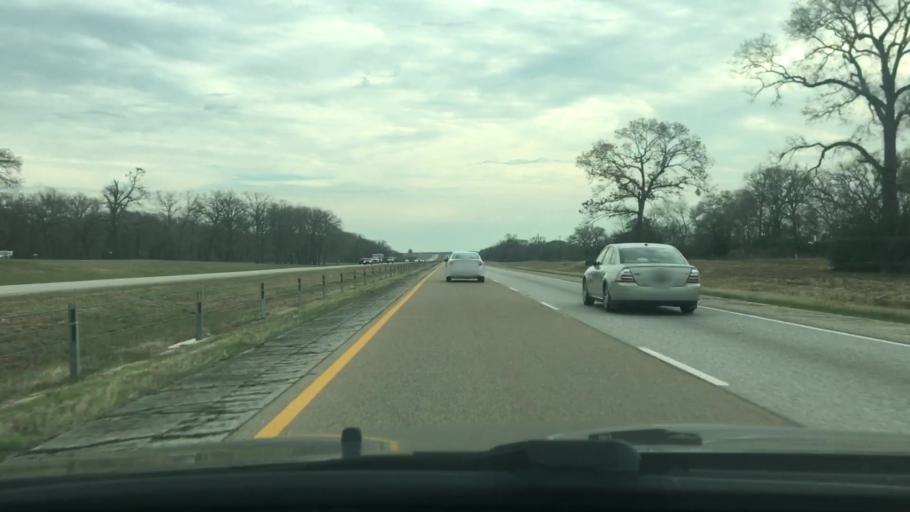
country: US
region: Texas
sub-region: Leon County
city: Centerville
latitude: 31.1380
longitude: -95.9801
